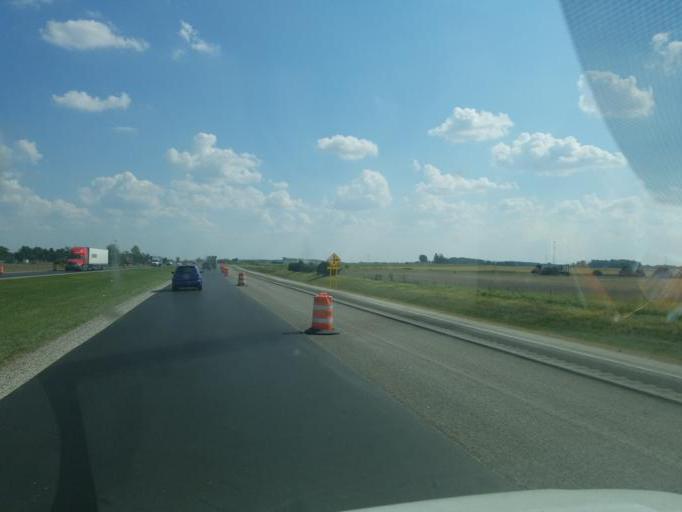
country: US
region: Ohio
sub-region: Van Wert County
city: Convoy
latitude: 40.9480
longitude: -84.7184
